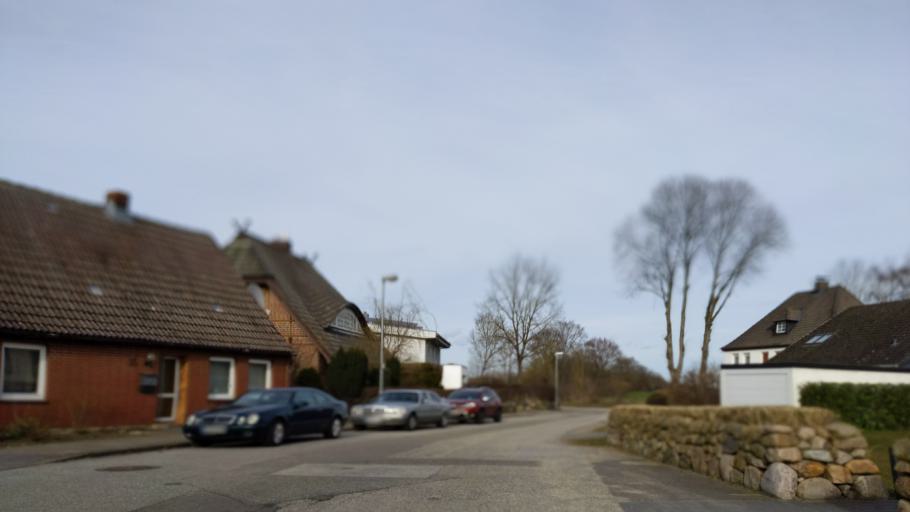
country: DE
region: Mecklenburg-Vorpommern
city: Selmsdorf
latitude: 53.9124
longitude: 10.8250
